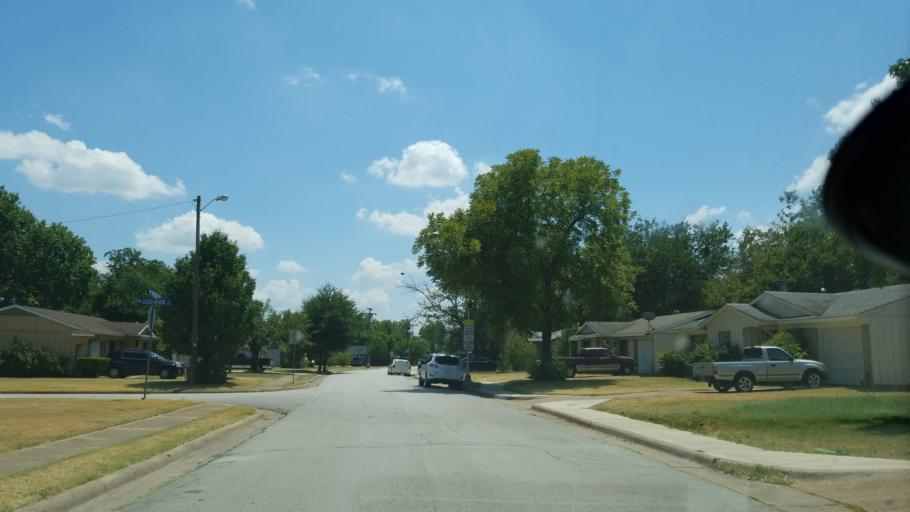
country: US
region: Texas
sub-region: Dallas County
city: Duncanville
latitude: 32.6674
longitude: -96.9011
